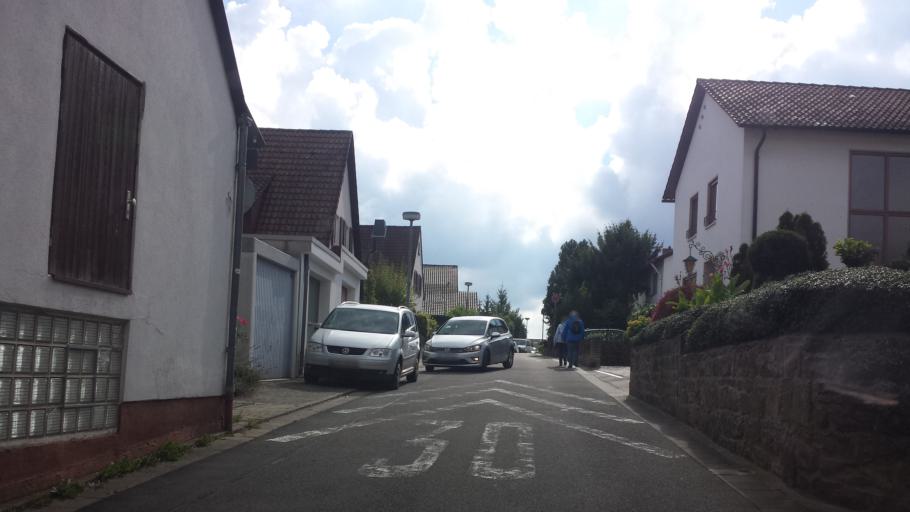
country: DE
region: Rheinland-Pfalz
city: Wachenheim
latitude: 49.4375
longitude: 8.1756
